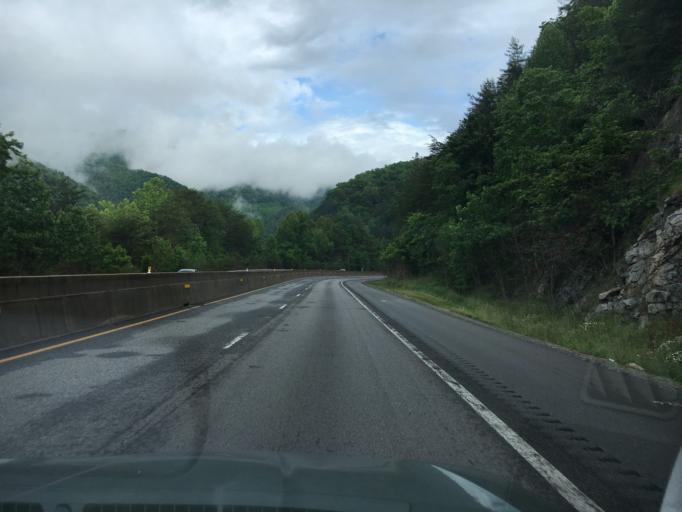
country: US
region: North Carolina
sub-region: Haywood County
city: Cove Creek
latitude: 35.7130
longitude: -83.0314
